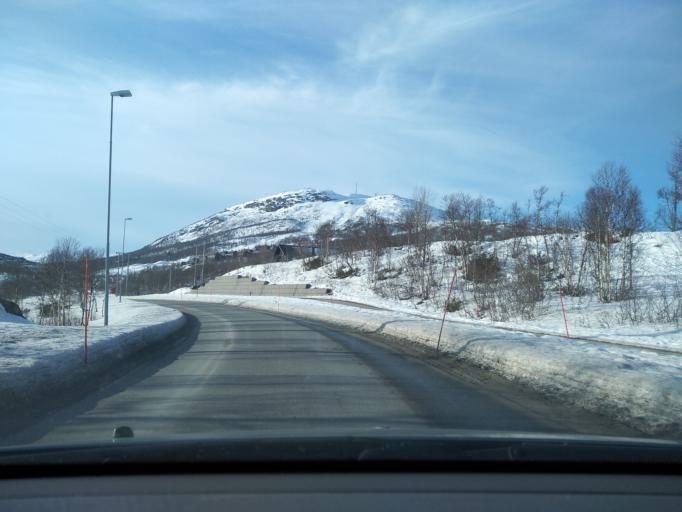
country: NO
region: Aust-Agder
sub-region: Bykle
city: Hovden
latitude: 59.5686
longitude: 7.3588
